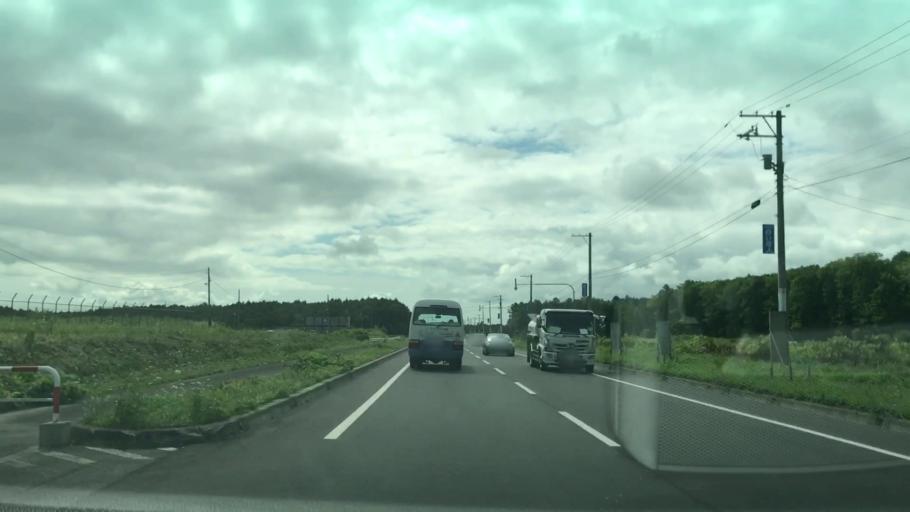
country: JP
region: Hokkaido
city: Chitose
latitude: 42.7720
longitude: 141.6791
